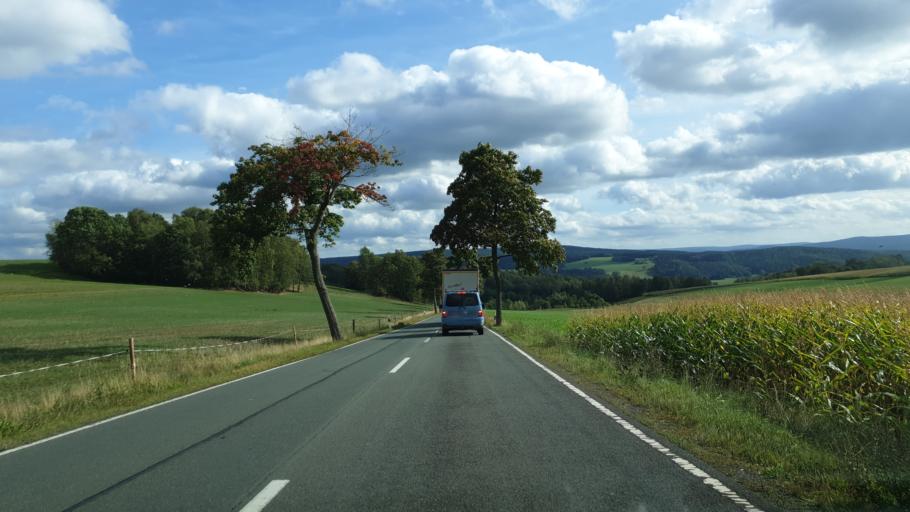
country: DE
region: Saxony
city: Lossnitz
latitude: 50.6448
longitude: 12.7296
